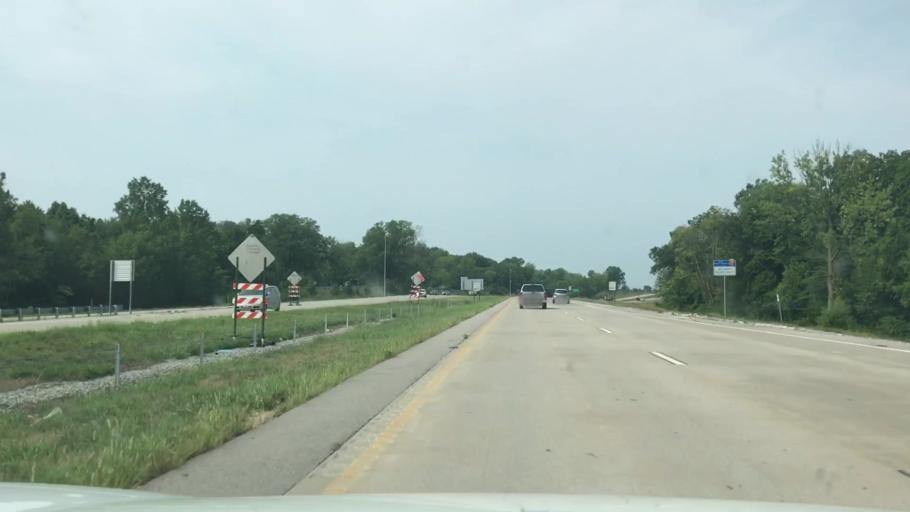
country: US
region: Missouri
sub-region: Saint Charles County
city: Cottleville
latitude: 38.7360
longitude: -90.6400
